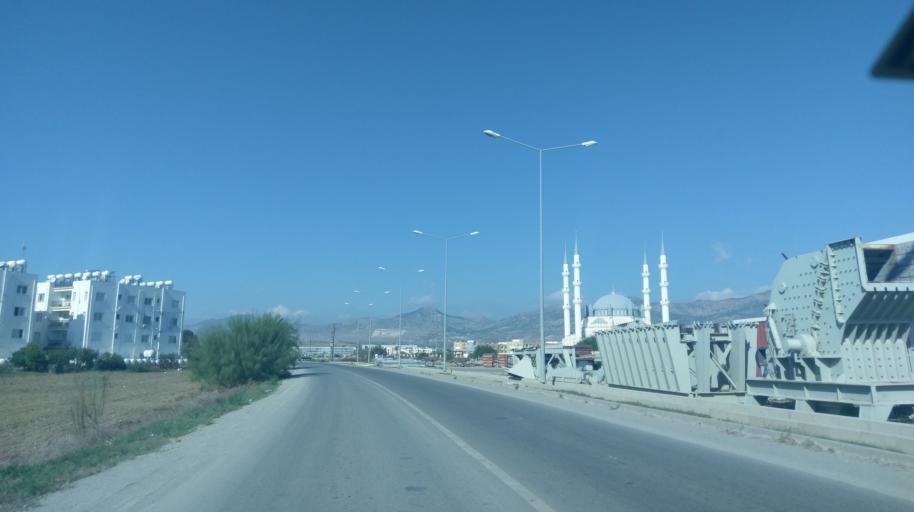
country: CY
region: Lefkosia
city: Nicosia
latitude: 35.2140
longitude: 33.4248
